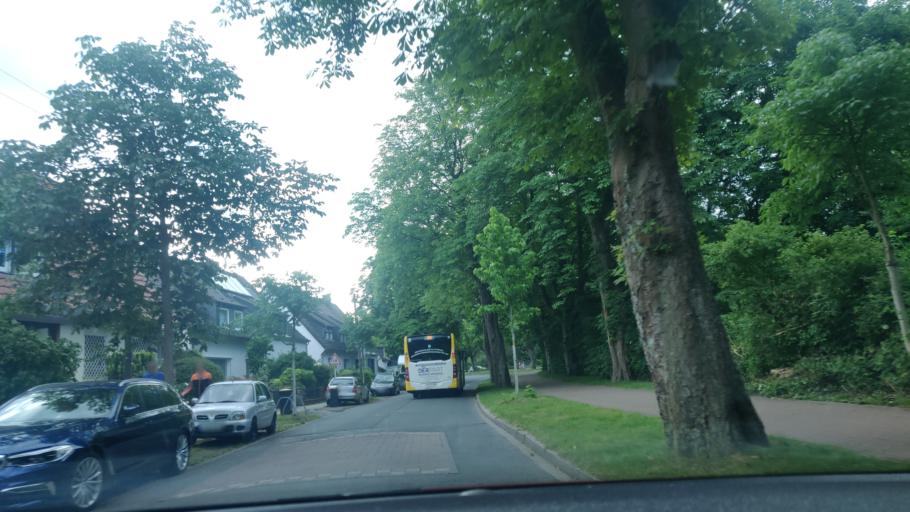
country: DE
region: North Rhine-Westphalia
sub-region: Regierungsbezirk Dusseldorf
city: Velbert
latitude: 51.3777
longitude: 7.0113
